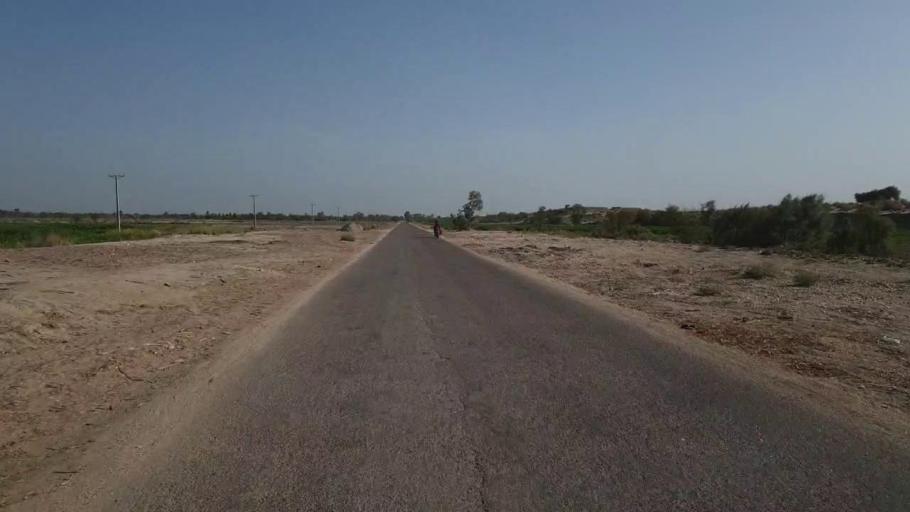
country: PK
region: Sindh
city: Daur
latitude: 26.4727
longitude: 68.4539
